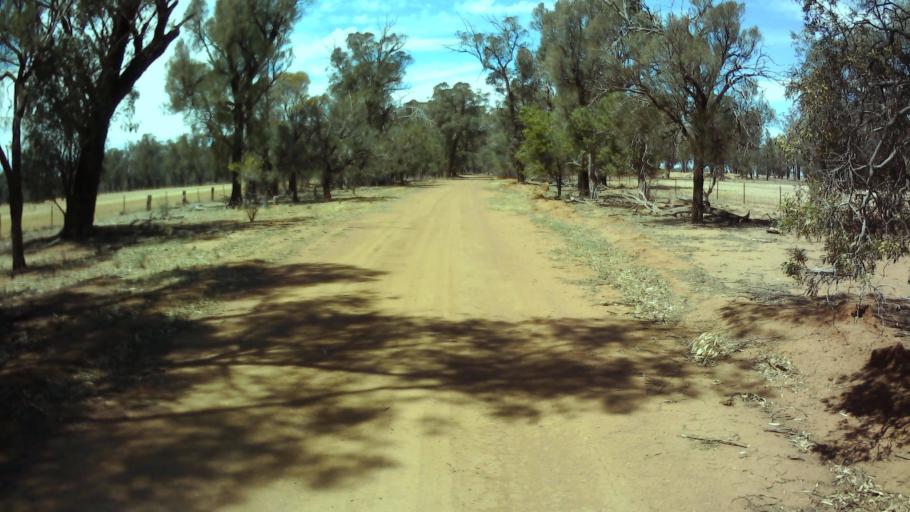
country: AU
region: New South Wales
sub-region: Weddin
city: Grenfell
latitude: -33.9091
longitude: 147.8068
